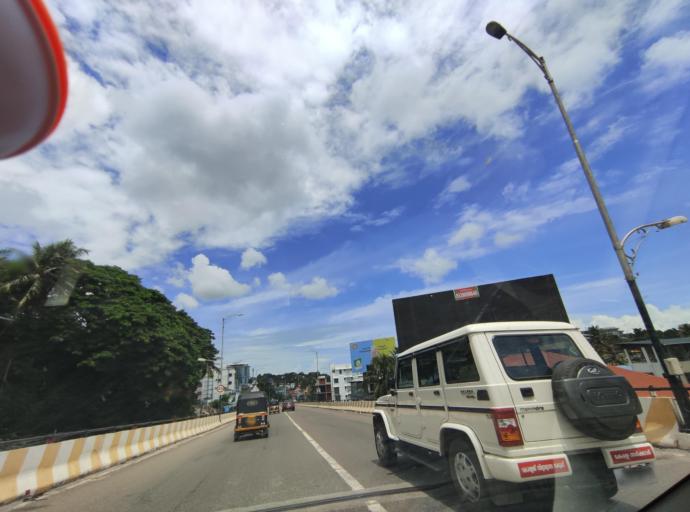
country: IN
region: Kerala
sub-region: Thiruvananthapuram
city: Thiruvananthapuram
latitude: 8.5003
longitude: 76.9543
